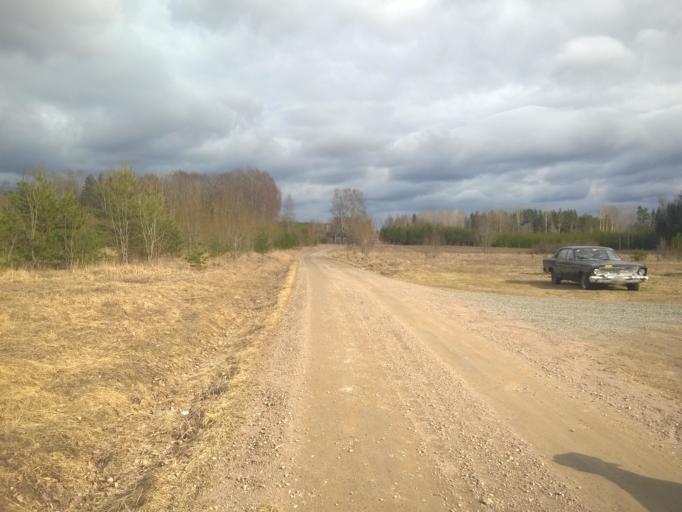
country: SE
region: Uppsala
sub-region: Osthammars Kommun
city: Bjorklinge
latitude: 60.1599
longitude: 17.5095
